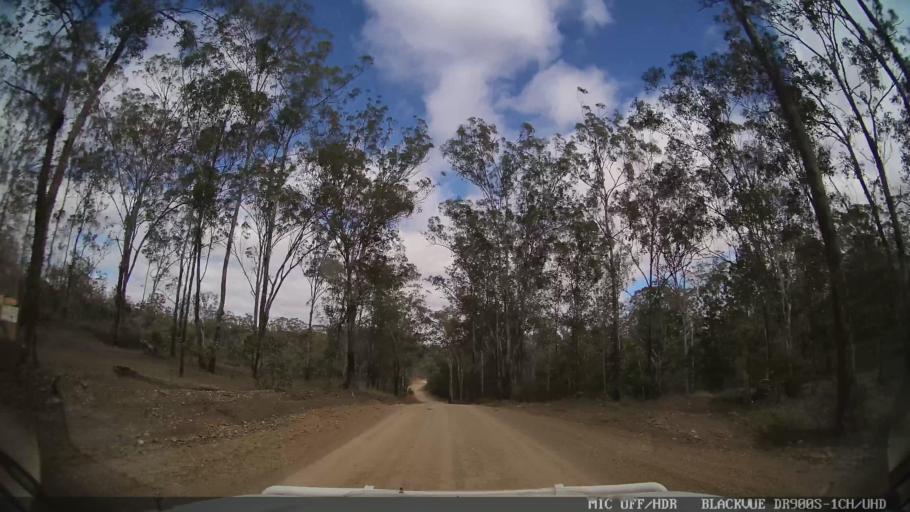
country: AU
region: Queensland
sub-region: Gladstone
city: Toolooa
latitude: -24.6831
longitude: 151.3310
